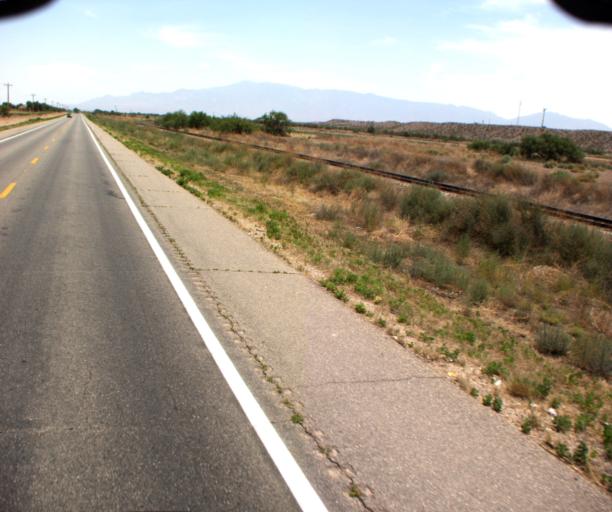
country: US
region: Arizona
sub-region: Graham County
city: Pima
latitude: 33.0030
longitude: -109.9447
